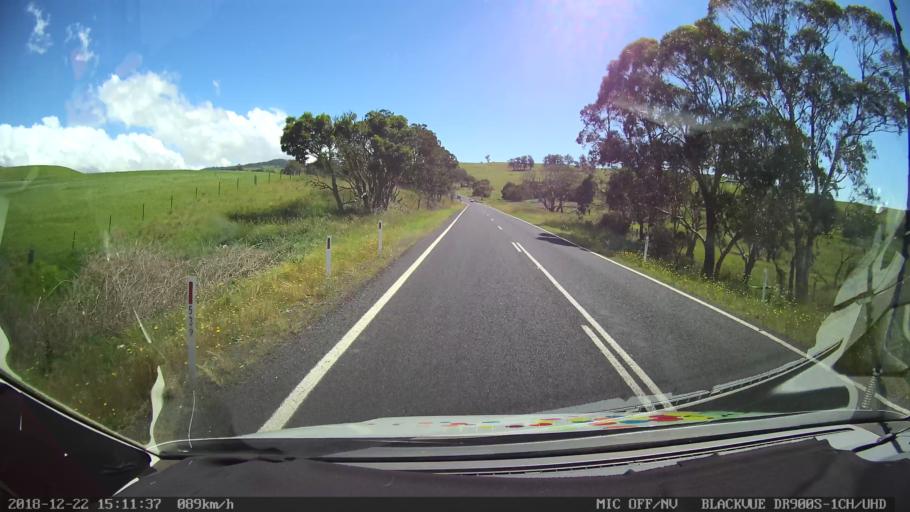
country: AU
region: New South Wales
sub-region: Bellingen
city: Dorrigo
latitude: -30.3458
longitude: 152.4009
